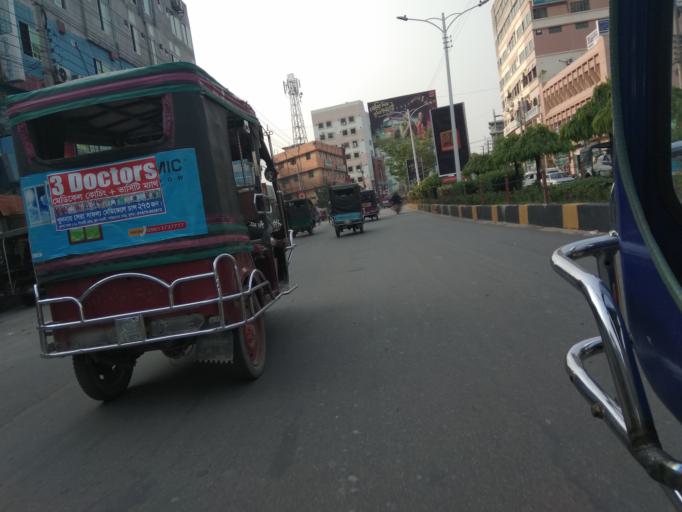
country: BD
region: Khulna
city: Khulna
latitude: 22.8149
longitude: 89.5548
